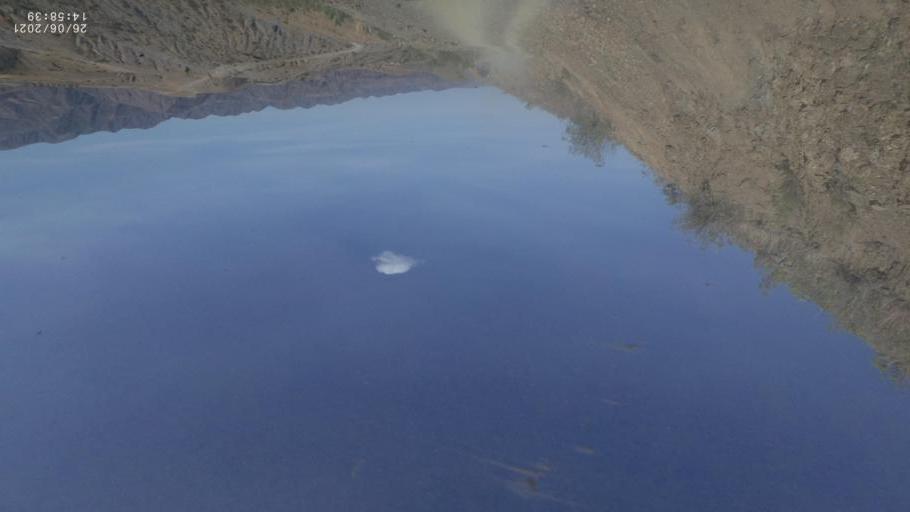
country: BO
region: Cochabamba
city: Mizque
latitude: -17.9451
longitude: -65.6193
